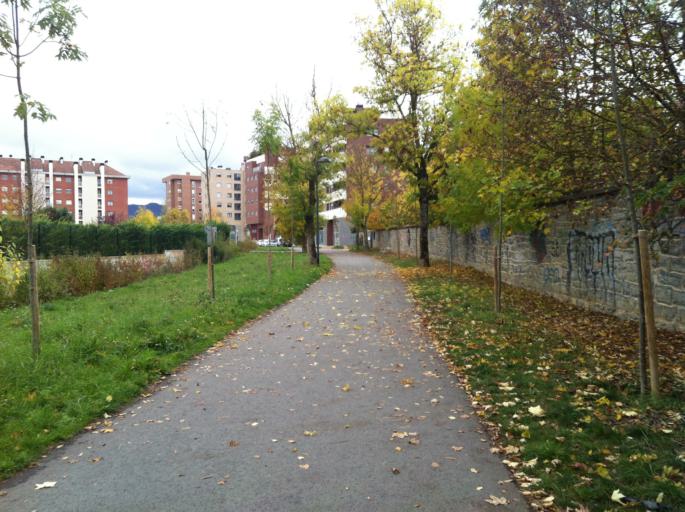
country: ES
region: Basque Country
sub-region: Provincia de Alava
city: Gasteiz / Vitoria
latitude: 42.8489
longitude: -2.6912
